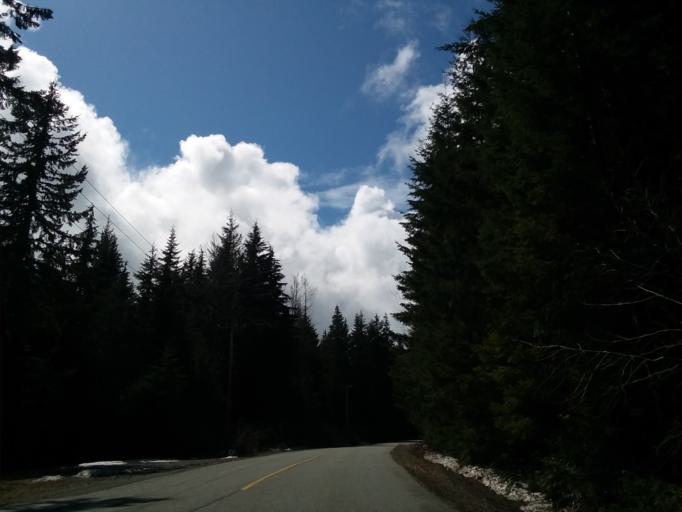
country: CA
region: British Columbia
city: Whistler
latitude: 50.1071
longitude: -122.9901
